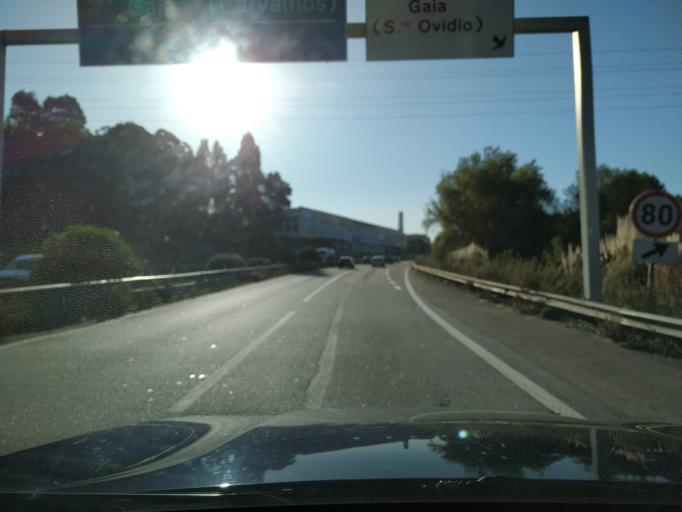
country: PT
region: Porto
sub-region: Vila Nova de Gaia
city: Vilar de Andorinho
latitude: 41.1094
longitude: -8.6063
